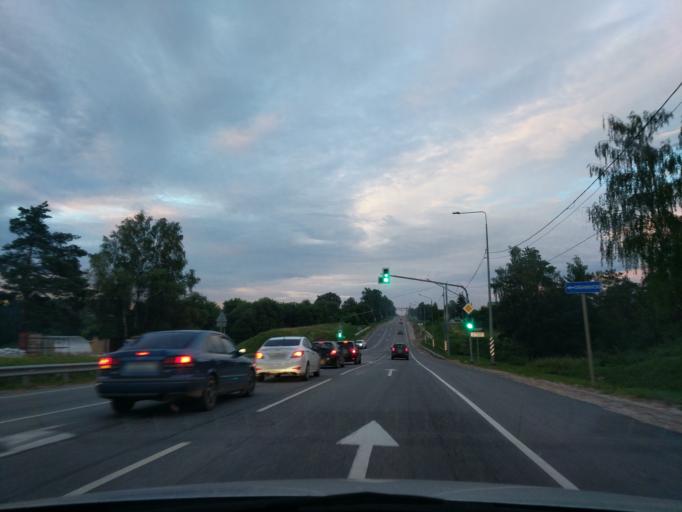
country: RU
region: Kaluga
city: Obninsk
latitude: 55.0705
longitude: 36.6102
